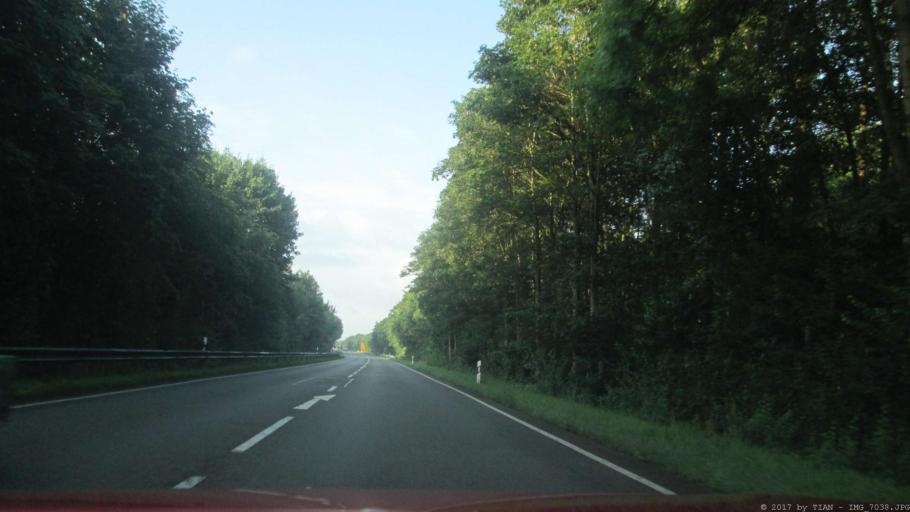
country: DE
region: Lower Saxony
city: Handorf
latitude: 53.3430
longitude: 10.3353
